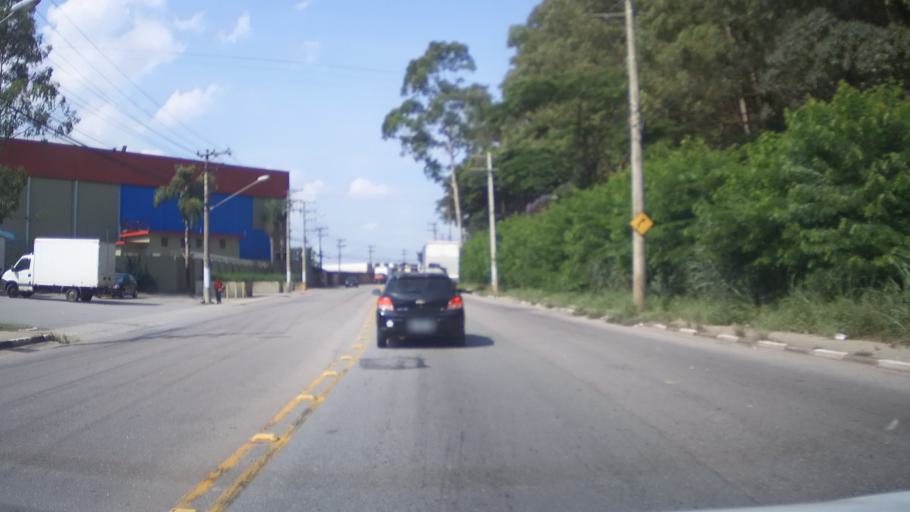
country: BR
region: Sao Paulo
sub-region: Guarulhos
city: Guarulhos
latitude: -23.4369
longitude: -46.4575
